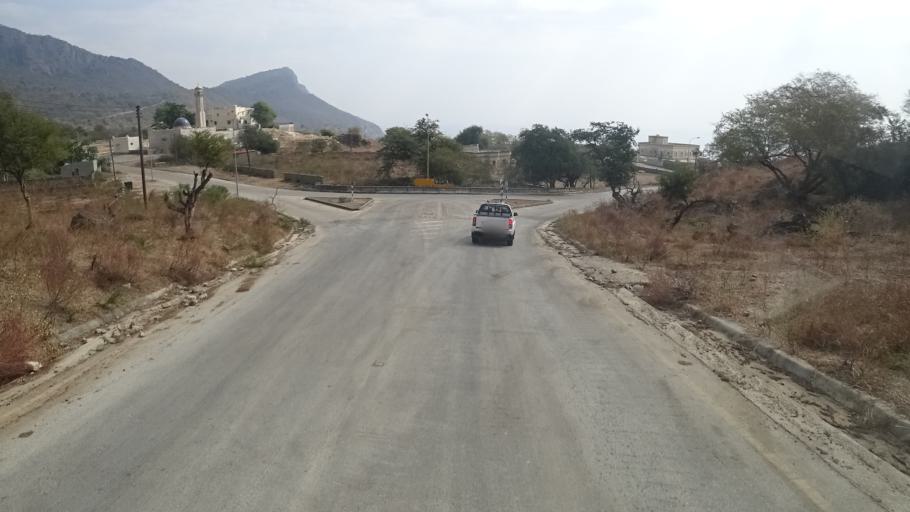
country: YE
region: Al Mahrah
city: Hawf
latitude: 16.7134
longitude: 53.2508
